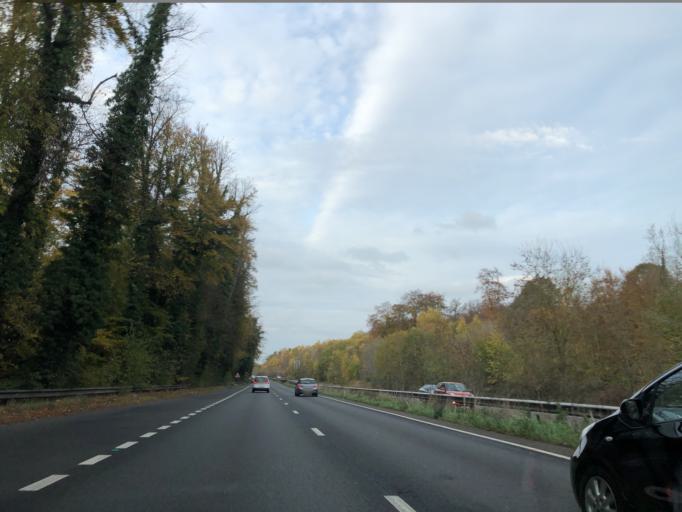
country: GB
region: England
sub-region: Royal Borough of Windsor and Maidenhead
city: Bisham
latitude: 51.5344
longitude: -0.7869
